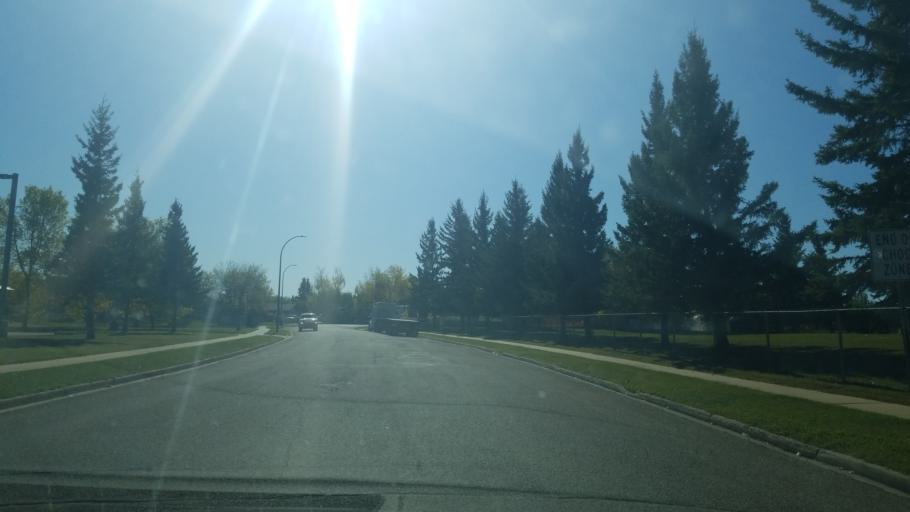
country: CA
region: Saskatchewan
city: Lloydminster
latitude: 53.2743
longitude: -110.0197
